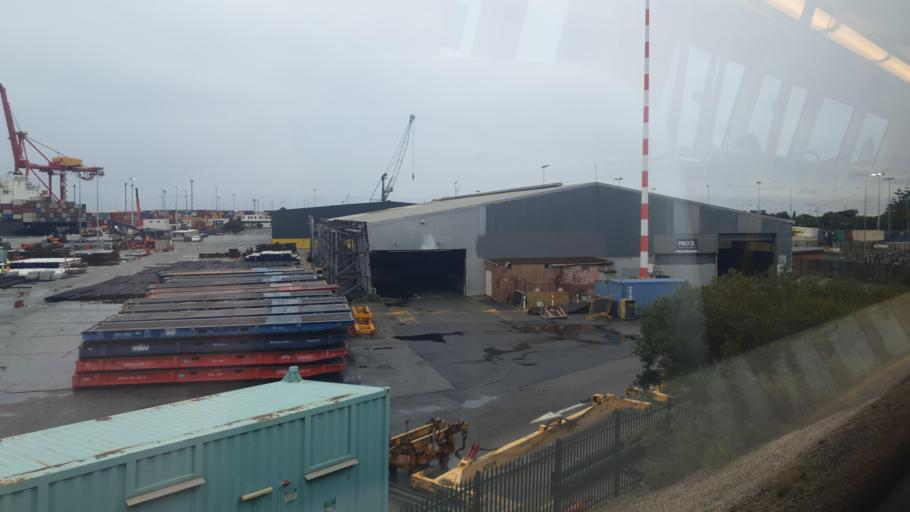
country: AU
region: Western Australia
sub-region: Fremantle
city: North Fremantle
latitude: -32.0387
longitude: 115.7537
